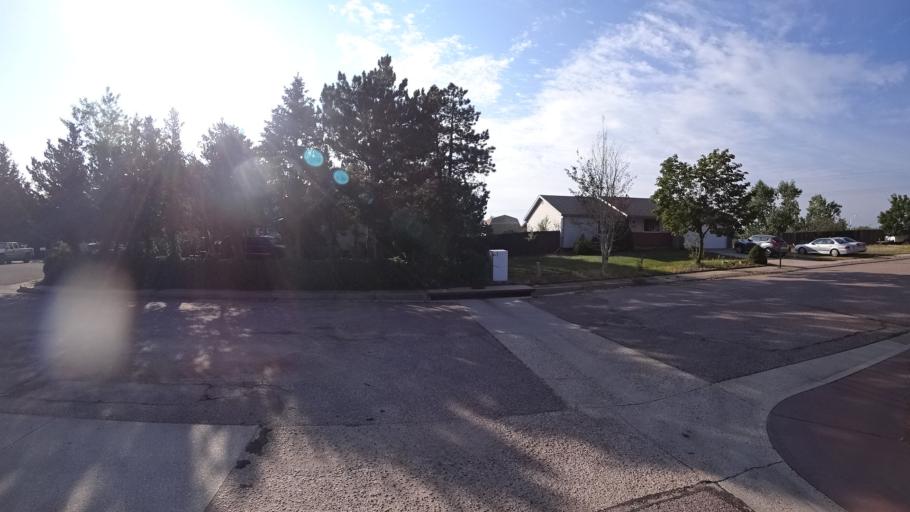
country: US
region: Colorado
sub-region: El Paso County
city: Colorado Springs
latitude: 38.8833
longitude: -104.7917
